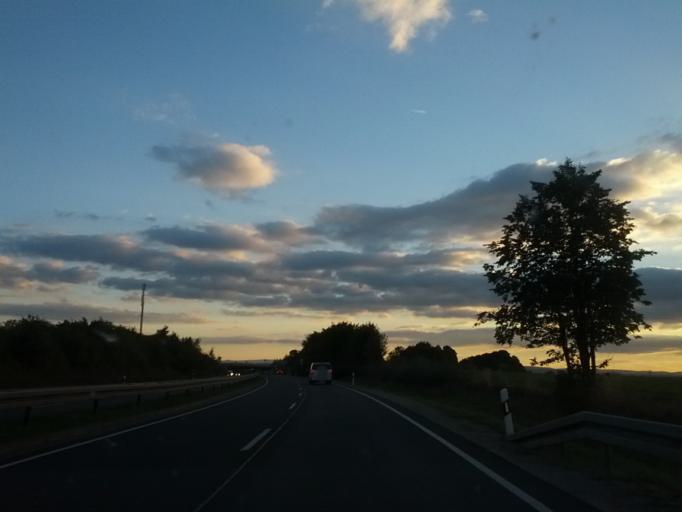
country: DE
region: Thuringia
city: Kirchheim
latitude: 50.9093
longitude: 11.0116
